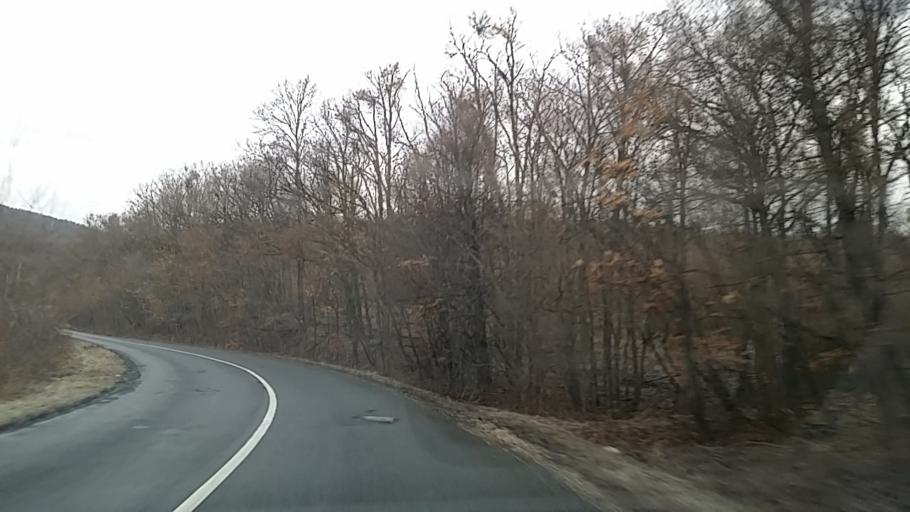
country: HU
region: Pest
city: Nagykovacsi
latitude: 47.7038
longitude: 19.0212
